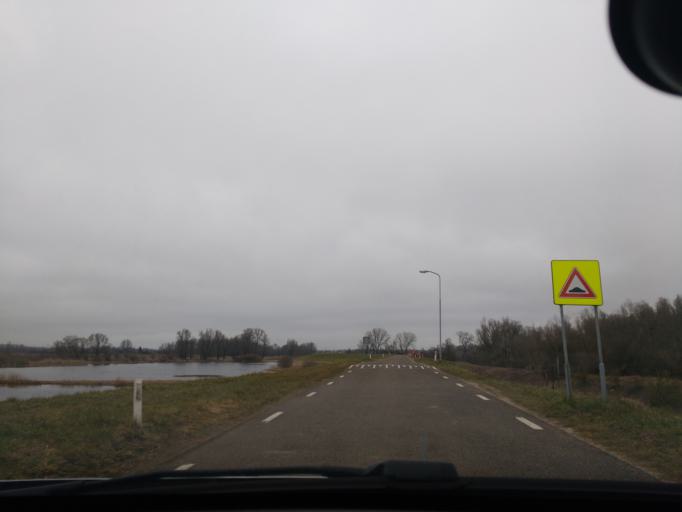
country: NL
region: Gelderland
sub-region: Gemeente Groesbeek
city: Berg en Dal
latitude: 51.8592
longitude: 5.9016
